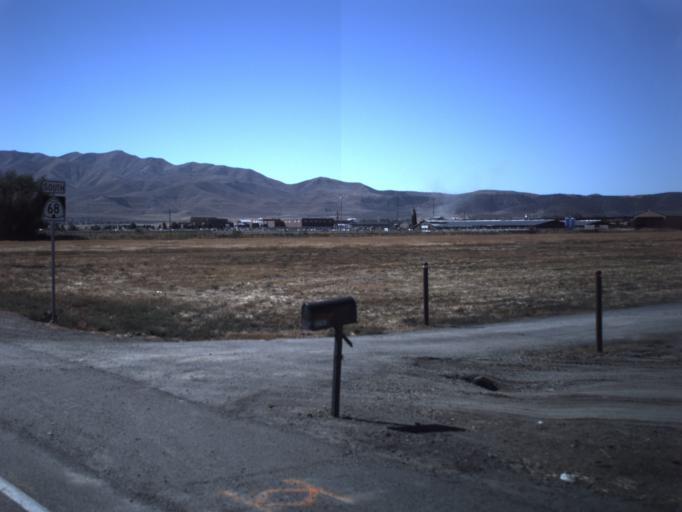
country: US
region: Utah
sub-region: Utah County
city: Saratoga Springs
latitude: 40.3721
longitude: -111.9165
